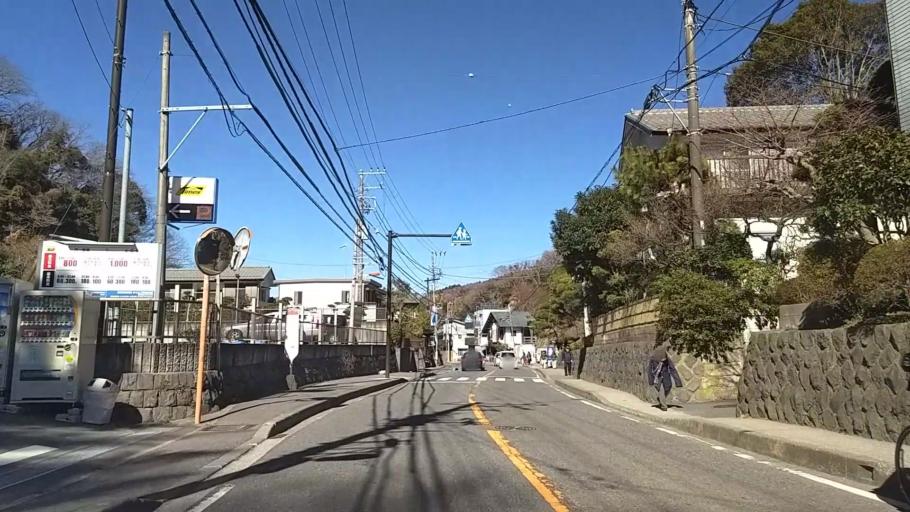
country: JP
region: Kanagawa
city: Kamakura
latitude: 35.3322
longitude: 139.5503
